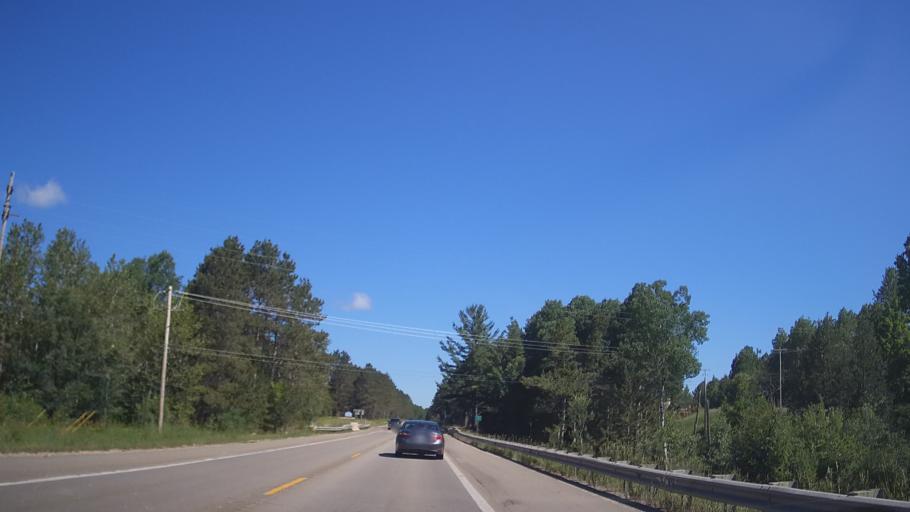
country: US
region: Michigan
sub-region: Cheboygan County
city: Indian River
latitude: 45.5391
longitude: -84.7827
